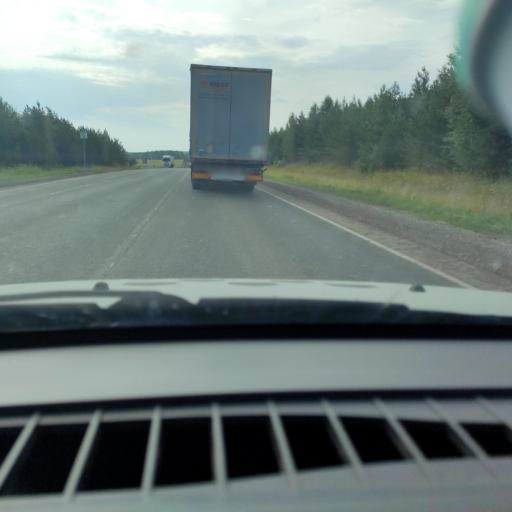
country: RU
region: Perm
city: Siva
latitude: 58.4176
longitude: 54.4623
